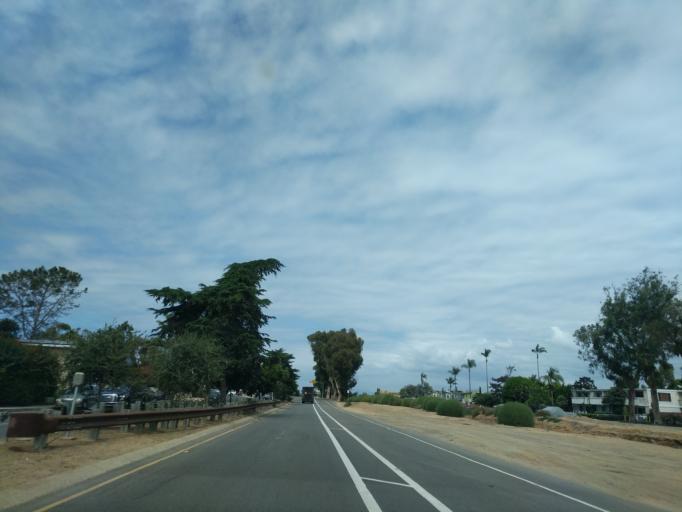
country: US
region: California
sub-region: San Diego County
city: Encinitas
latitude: 33.0794
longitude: -117.3072
